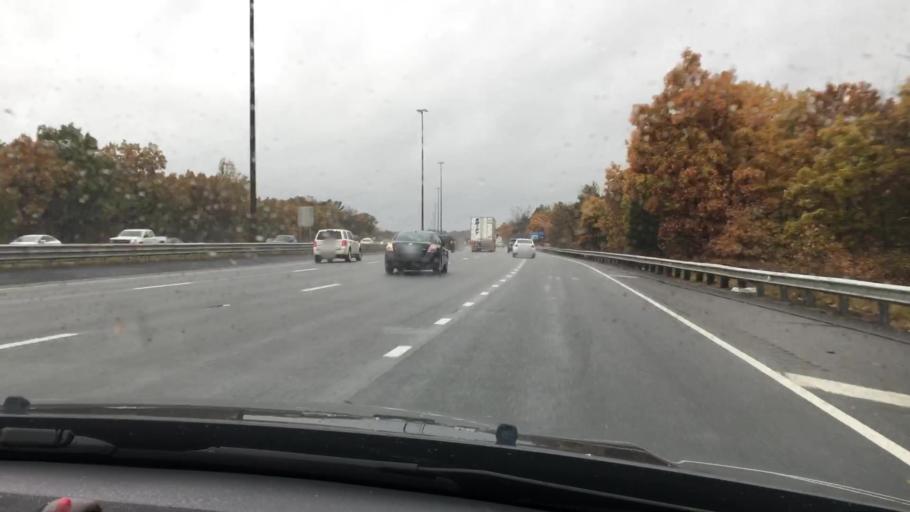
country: US
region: Massachusetts
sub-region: Middlesex County
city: Chelmsford
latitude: 42.6069
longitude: -71.3375
